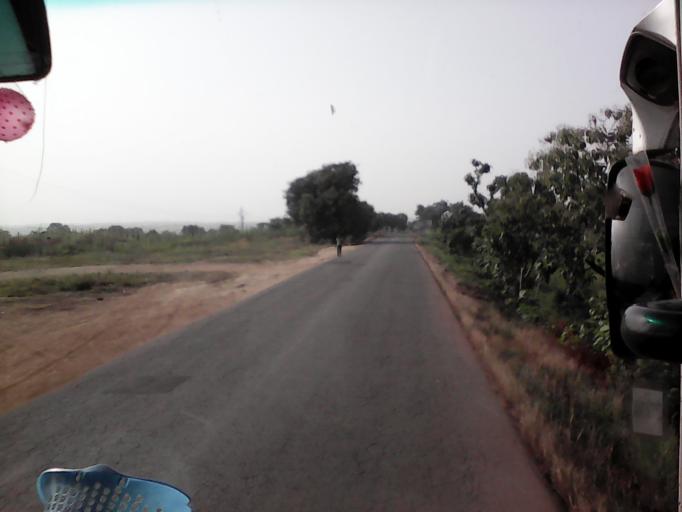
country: TG
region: Kara
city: Kara
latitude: 9.5192
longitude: 1.2087
